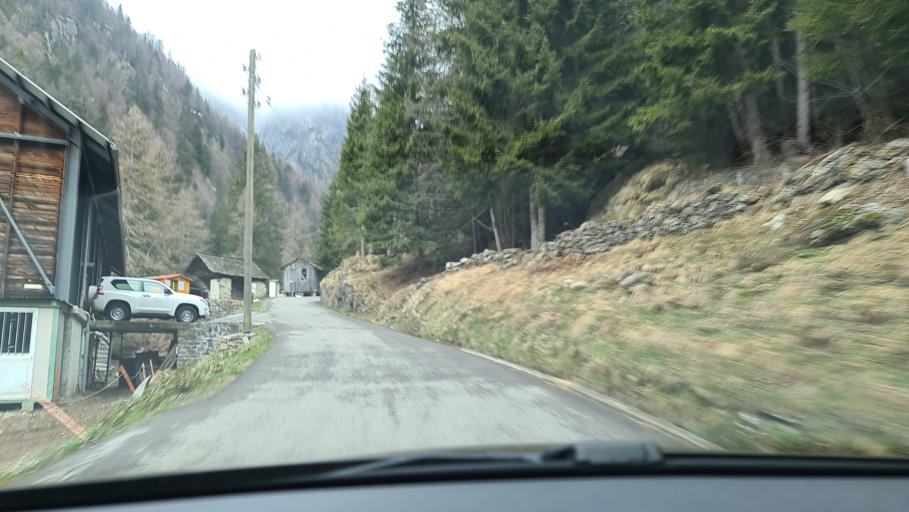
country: CH
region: Ticino
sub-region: Leventina District
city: Airolo
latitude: 46.4471
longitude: 8.6639
